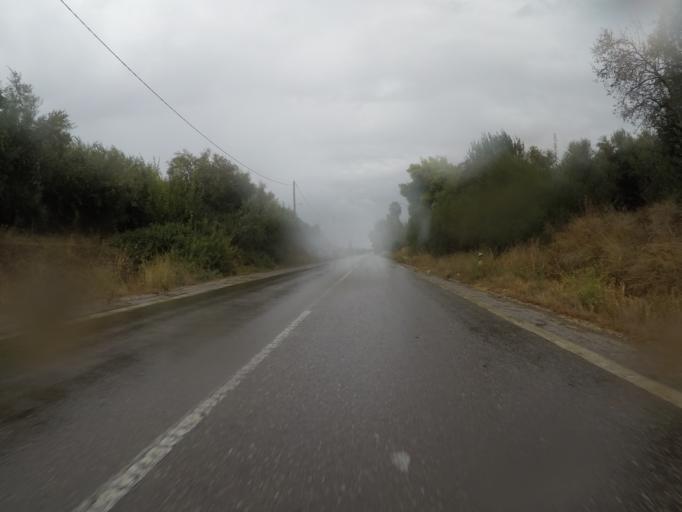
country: GR
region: West Greece
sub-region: Nomos Ileias
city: Zacharo
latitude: 37.3989
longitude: 21.6814
